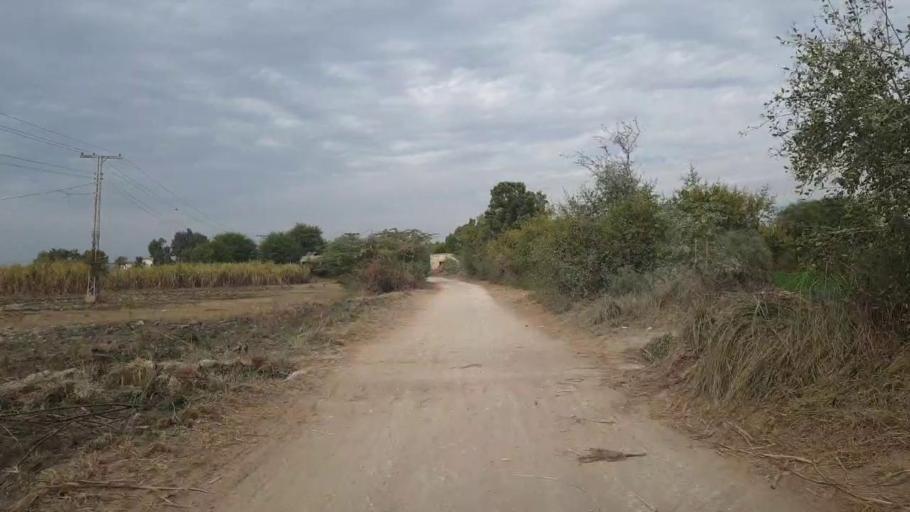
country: PK
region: Sindh
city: Sinjhoro
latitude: 26.0301
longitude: 68.8739
